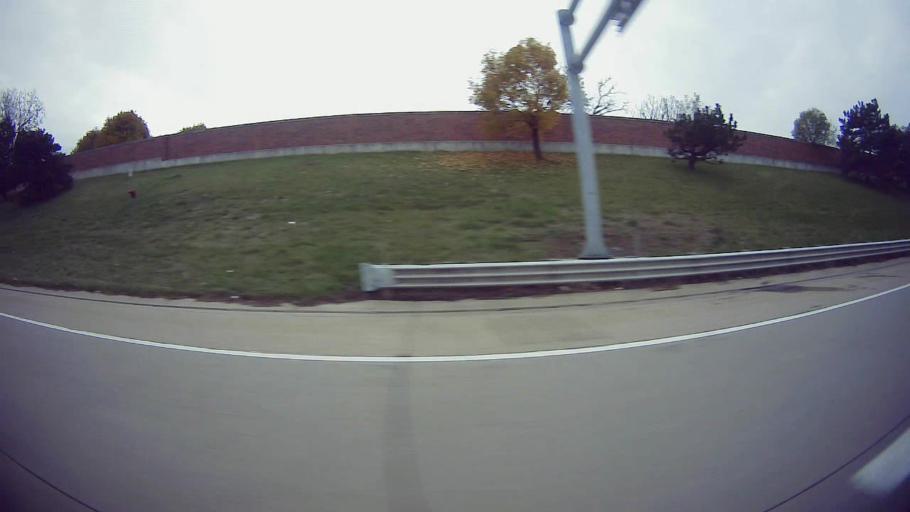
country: US
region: Michigan
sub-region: Oakland County
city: Lathrup Village
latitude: 42.4859
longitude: -83.2526
